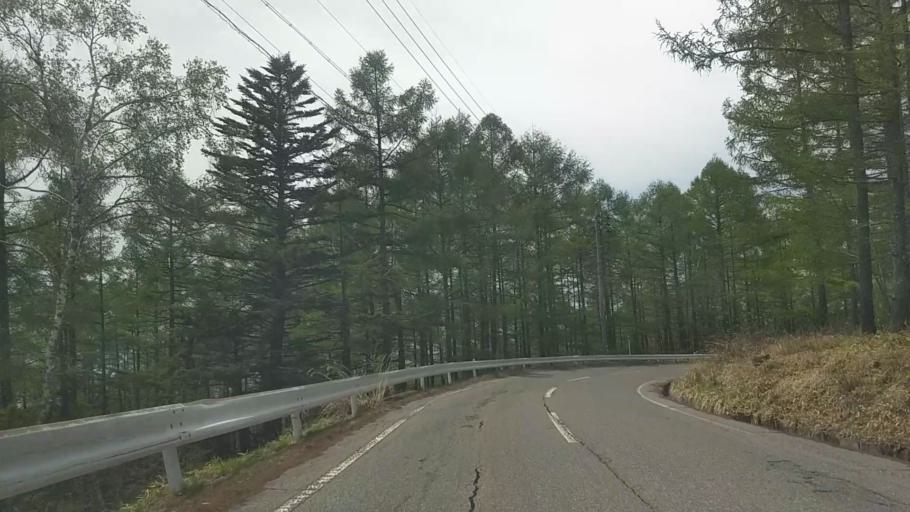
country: JP
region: Nagano
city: Chino
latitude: 36.0460
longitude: 138.3083
